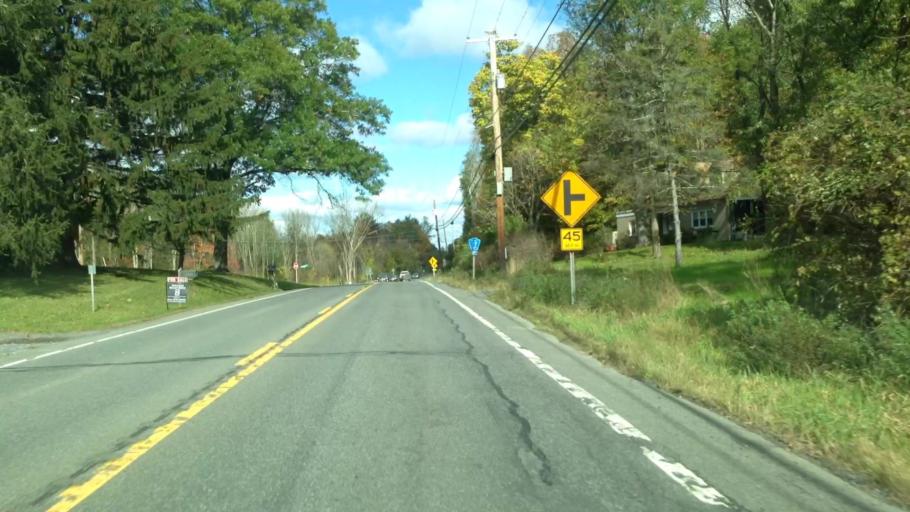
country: US
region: New York
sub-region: Ulster County
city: New Paltz
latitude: 41.7803
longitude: -74.0727
